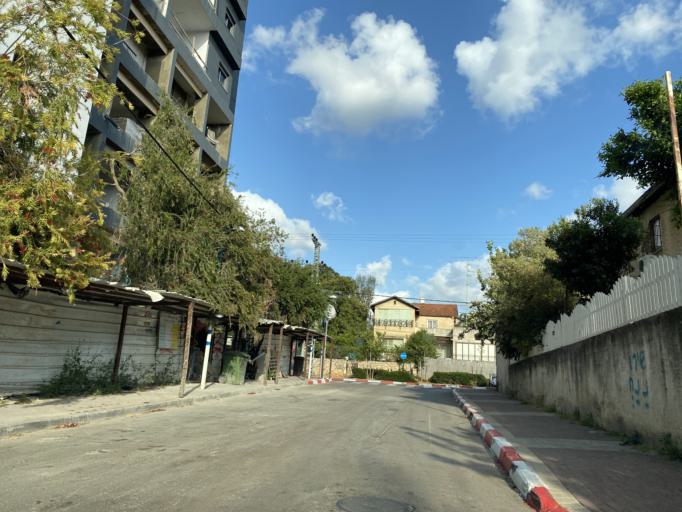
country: IL
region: Central District
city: Kfar Saba
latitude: 32.1775
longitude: 34.9176
